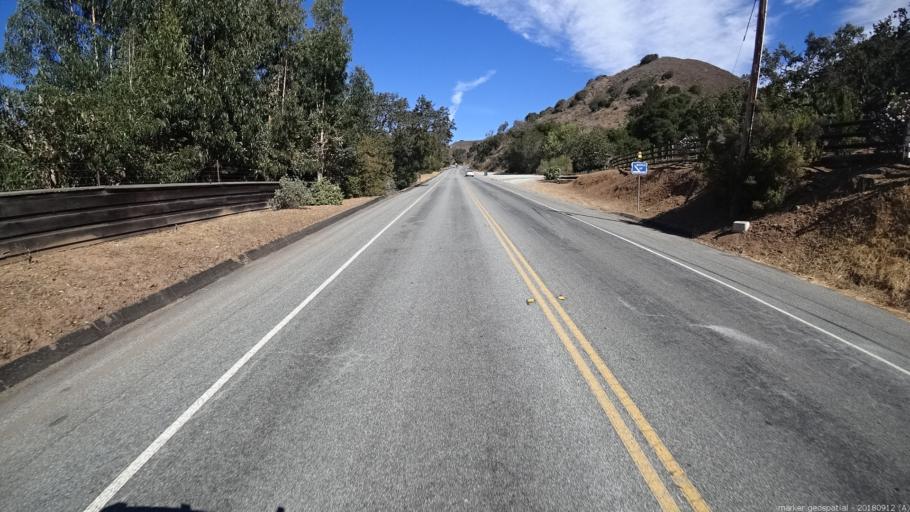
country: US
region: California
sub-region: Monterey County
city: Carmel Valley Village
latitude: 36.5097
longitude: -121.7541
